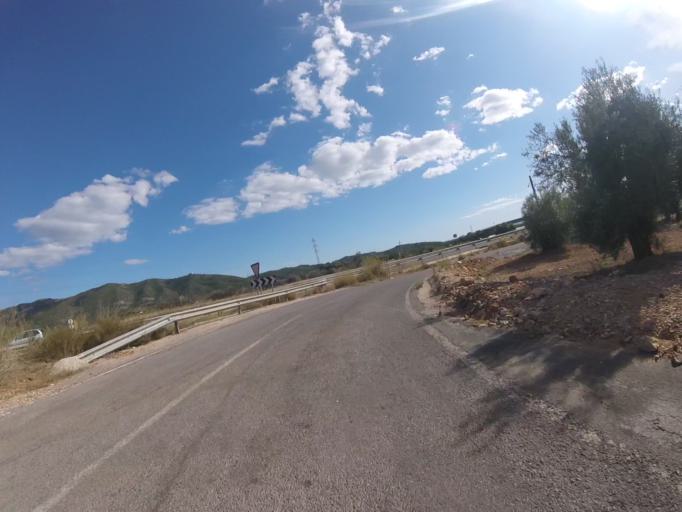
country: ES
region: Valencia
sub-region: Provincia de Castello
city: Alcala de Xivert
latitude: 40.2697
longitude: 0.2403
